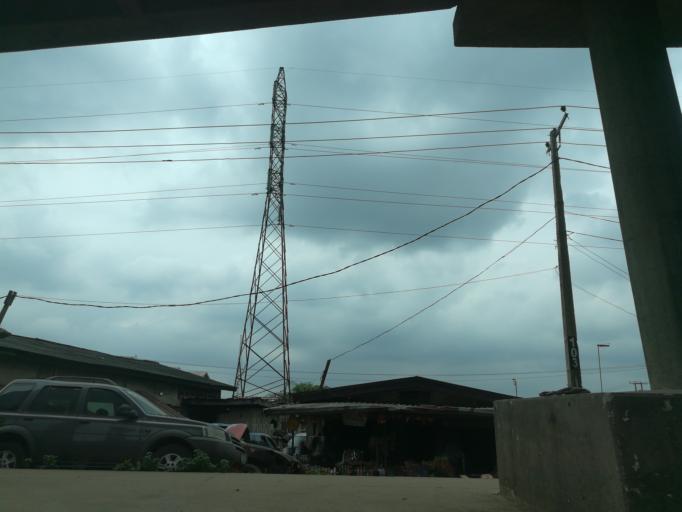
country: NG
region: Lagos
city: Ojota
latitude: 6.6118
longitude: 3.4151
